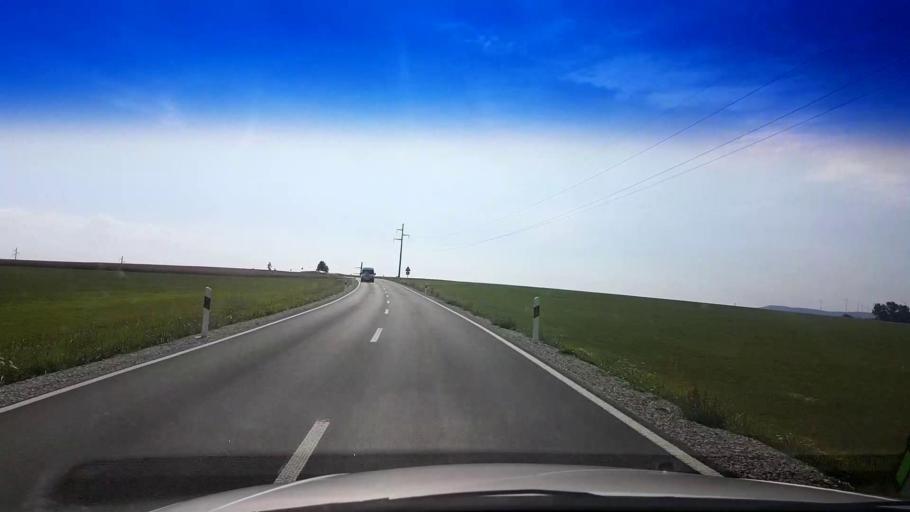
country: DE
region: Bavaria
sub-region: Upper Franconia
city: Mistelgau
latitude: 49.9366
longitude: 11.4664
